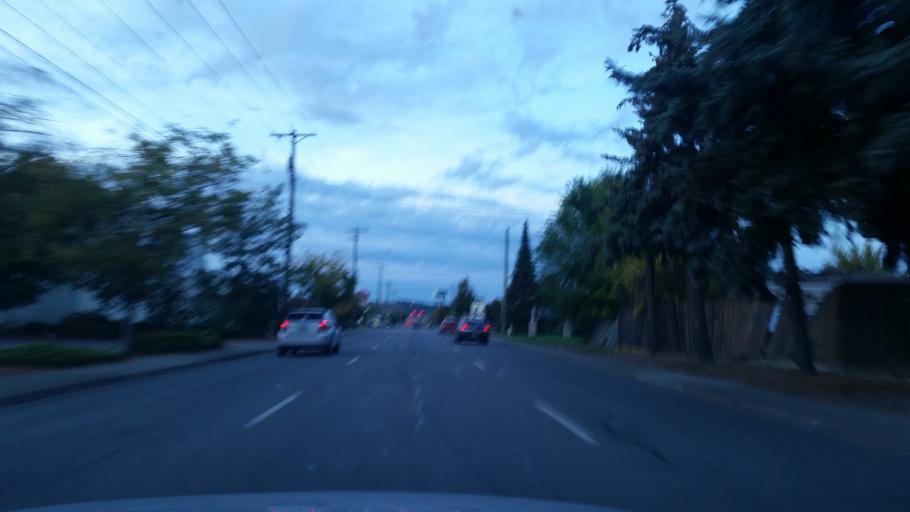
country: US
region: Washington
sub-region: Spokane County
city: Dishman
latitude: 47.6679
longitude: -117.2816
